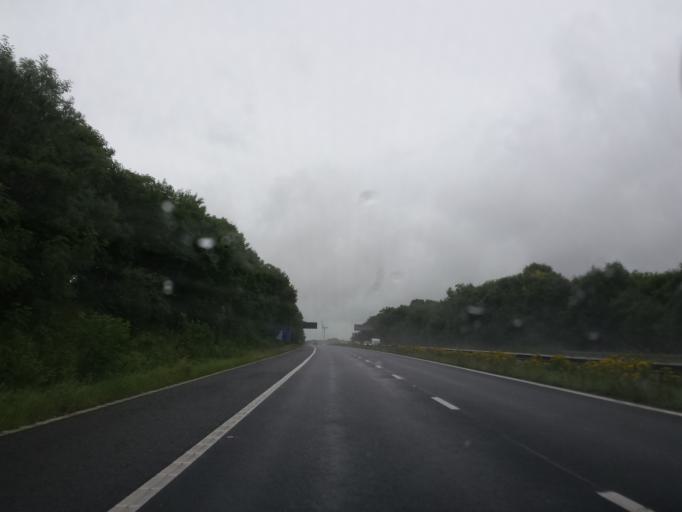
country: GB
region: England
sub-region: Rotherham
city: Bramley
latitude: 53.3935
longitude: -1.2721
